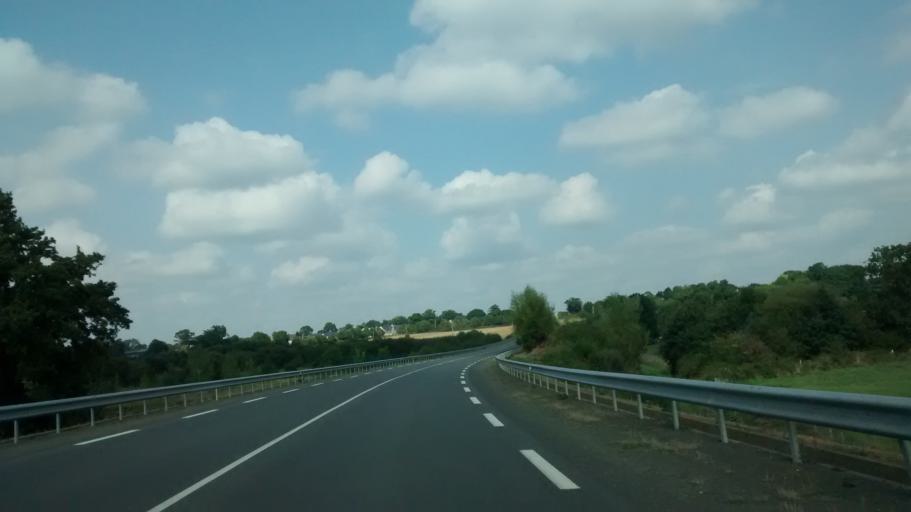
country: FR
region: Brittany
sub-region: Departement d'Ille-et-Vilaine
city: Saint-Aubin-du-Cormier
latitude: 48.2496
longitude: -1.4091
